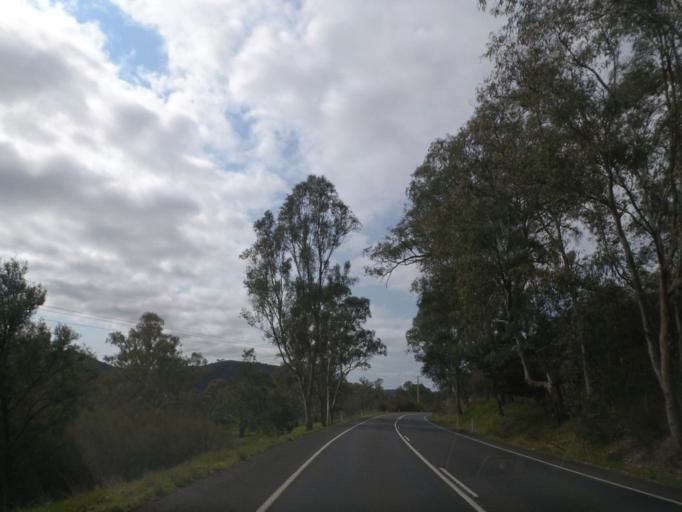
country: AU
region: Victoria
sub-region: Murrindindi
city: Kinglake West
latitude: -37.1439
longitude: 145.2497
